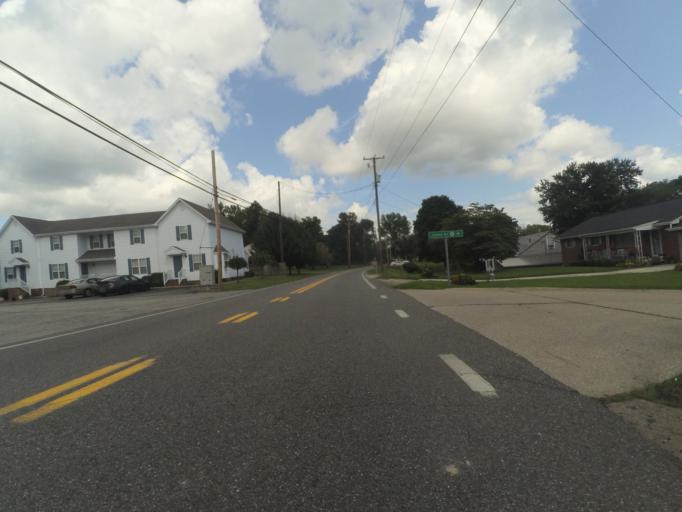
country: US
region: West Virginia
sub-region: Cabell County
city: Pea Ridge
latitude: 38.4175
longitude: -82.3112
